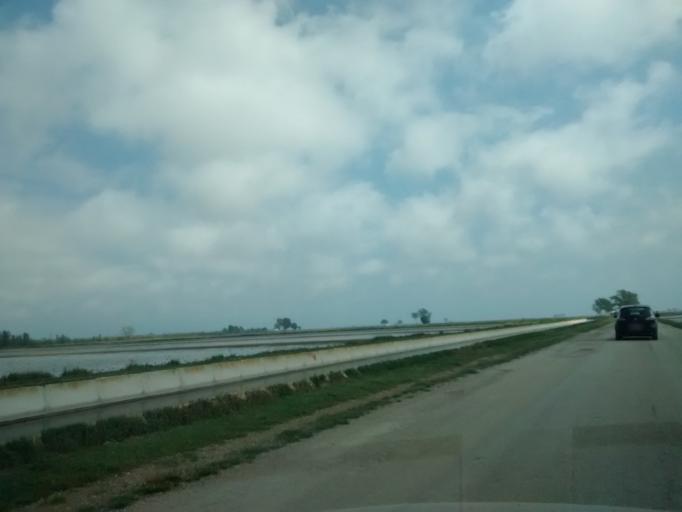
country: ES
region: Catalonia
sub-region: Provincia de Tarragona
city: Deltebre
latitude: 40.6909
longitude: 0.7796
